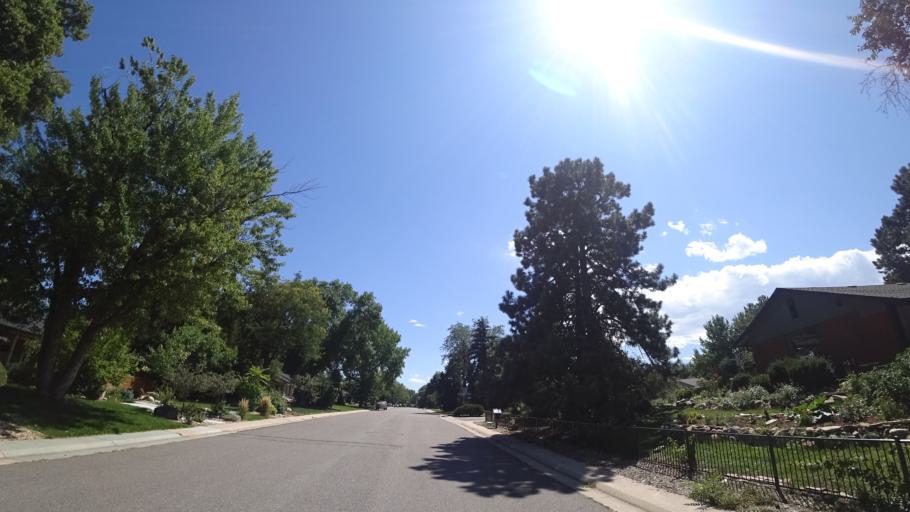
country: US
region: Colorado
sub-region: Arapahoe County
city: Greenwood Village
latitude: 39.6075
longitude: -104.9768
